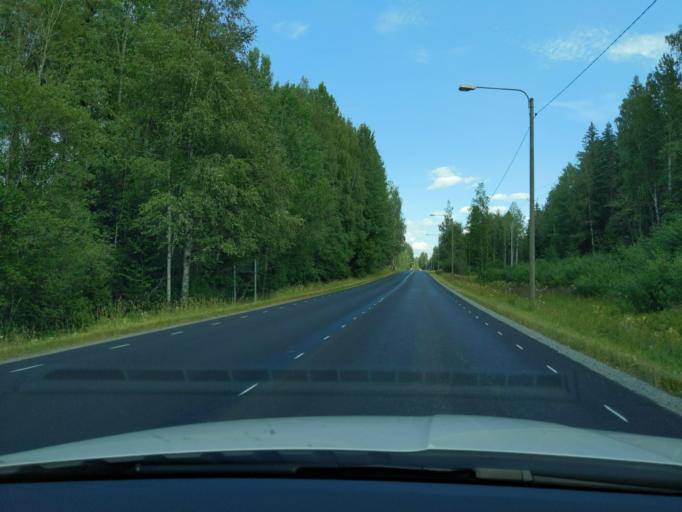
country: FI
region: Paijanne Tavastia
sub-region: Lahti
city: Lahti
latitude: 61.0295
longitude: 25.7353
